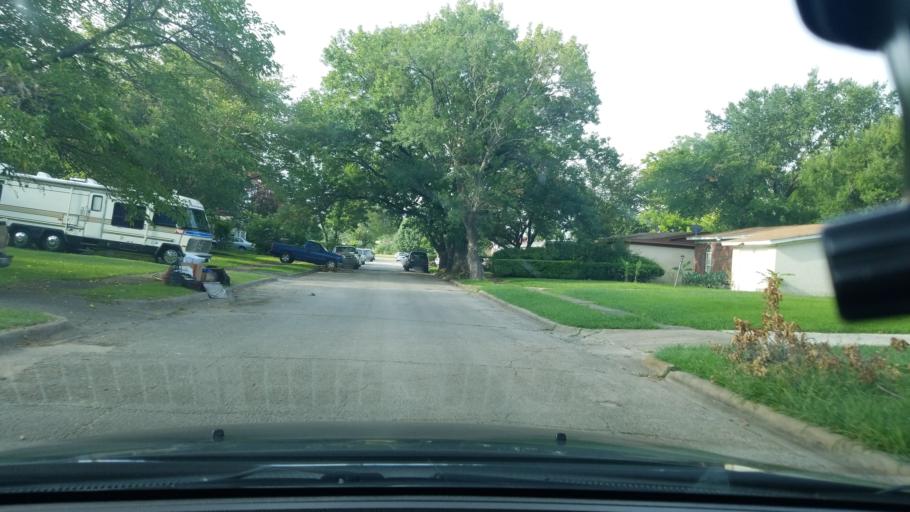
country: US
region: Texas
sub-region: Dallas County
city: Mesquite
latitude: 32.8230
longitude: -96.6586
